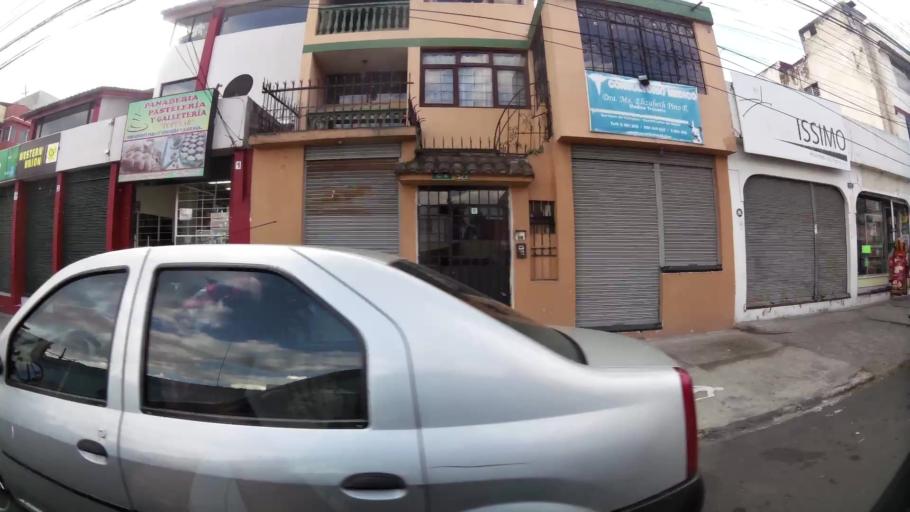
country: EC
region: Pichincha
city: Quito
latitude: -0.1401
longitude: -78.4767
